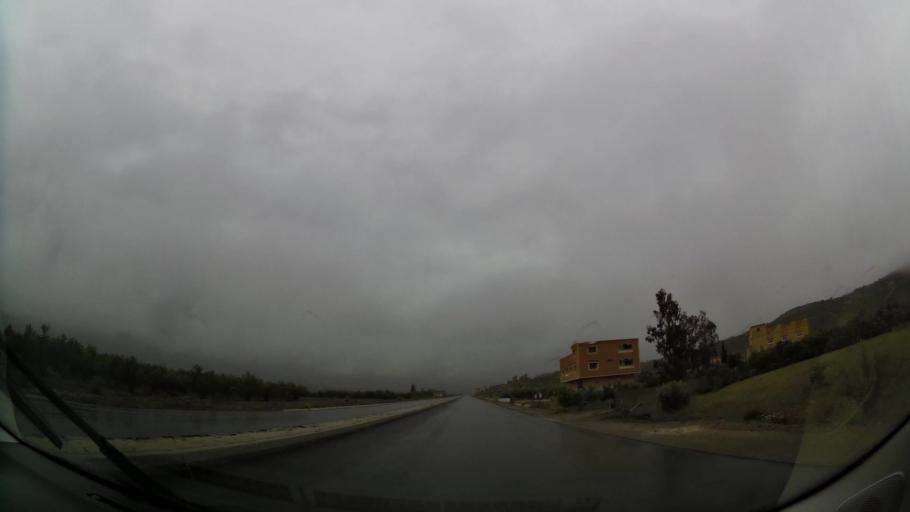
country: MA
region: Oriental
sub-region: Nador
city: Midar
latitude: 34.8353
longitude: -3.7201
